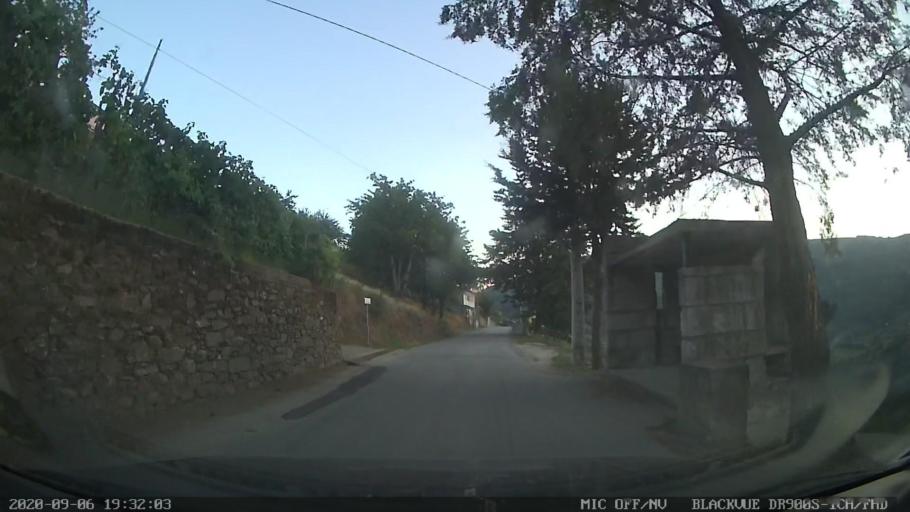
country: PT
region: Vila Real
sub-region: Mesao Frio
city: Mesao Frio
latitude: 41.1806
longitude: -7.9015
